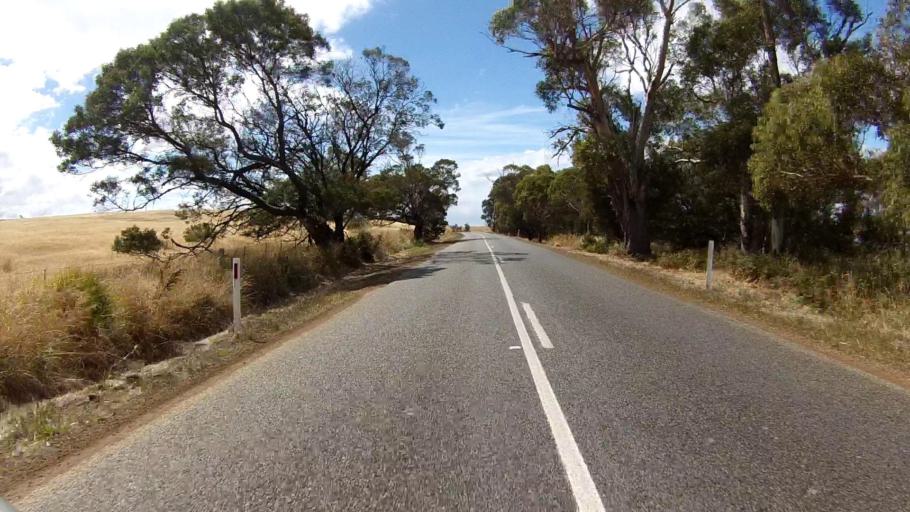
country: AU
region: Tasmania
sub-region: Sorell
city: Sorell
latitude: -42.2803
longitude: 148.0005
